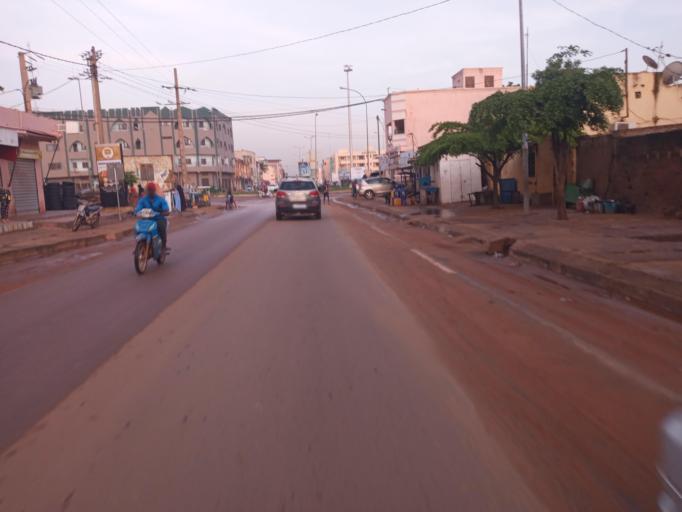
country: ML
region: Bamako
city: Bamako
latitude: 12.6277
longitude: -8.0362
